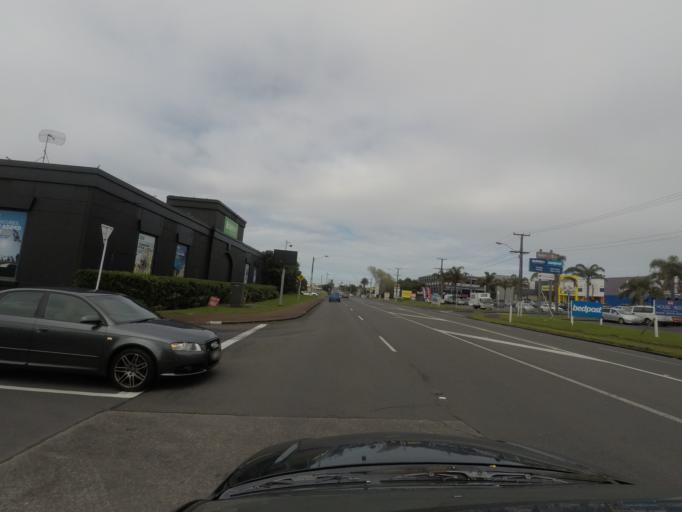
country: NZ
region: Auckland
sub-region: Auckland
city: Tamaki
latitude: -36.8995
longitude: 174.8443
